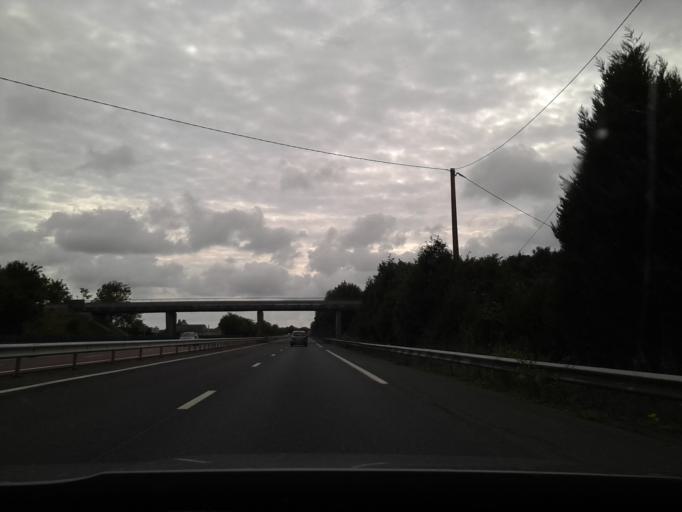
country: FR
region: Lower Normandy
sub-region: Departement du Calvados
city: Grandcamp-Maisy
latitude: 49.3426
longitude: -1.0419
